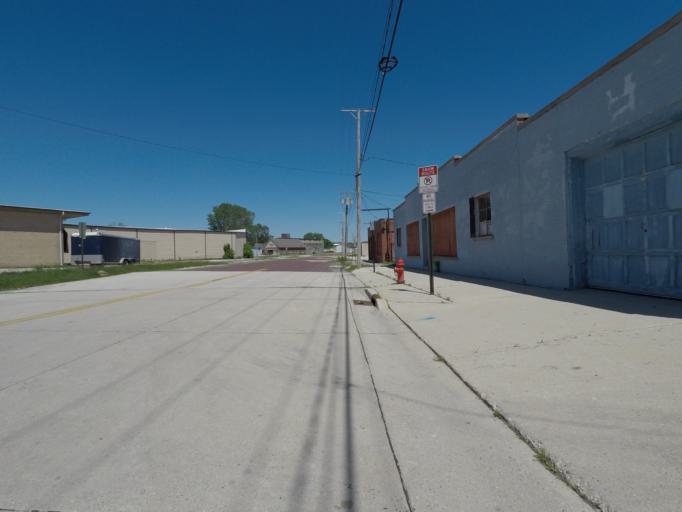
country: US
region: Wisconsin
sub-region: Sheboygan County
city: Sheboygan
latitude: 43.7500
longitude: -87.7187
